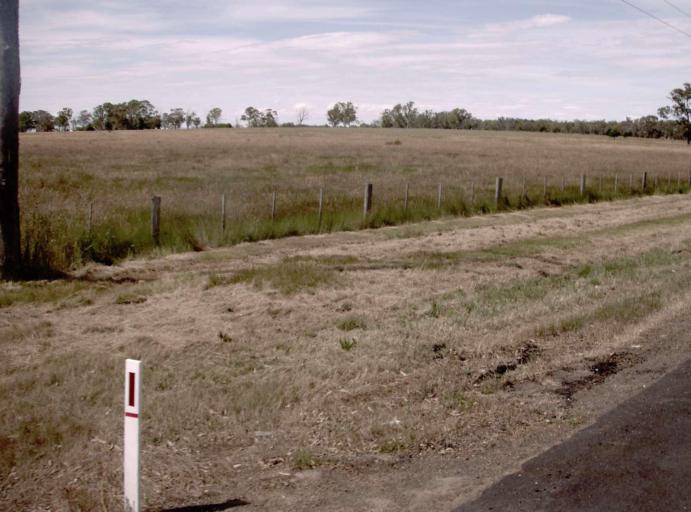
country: AU
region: Victoria
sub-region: Wellington
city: Sale
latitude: -37.9242
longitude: 147.2336
